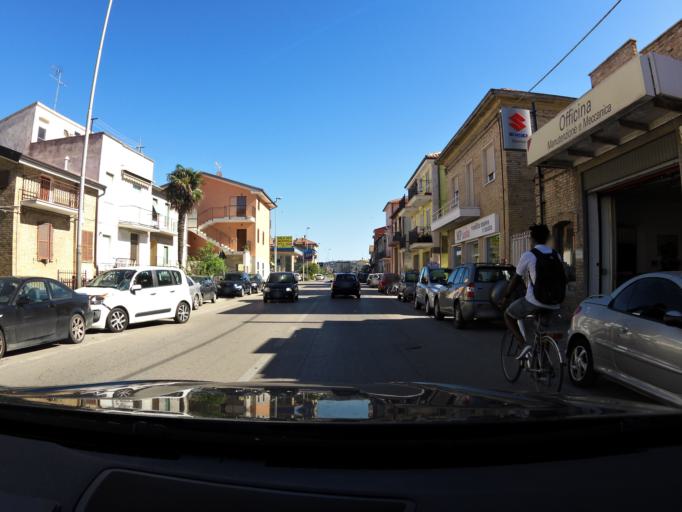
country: IT
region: The Marches
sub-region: Province of Fermo
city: Porto San Giorgio
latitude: 43.1731
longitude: 13.7968
